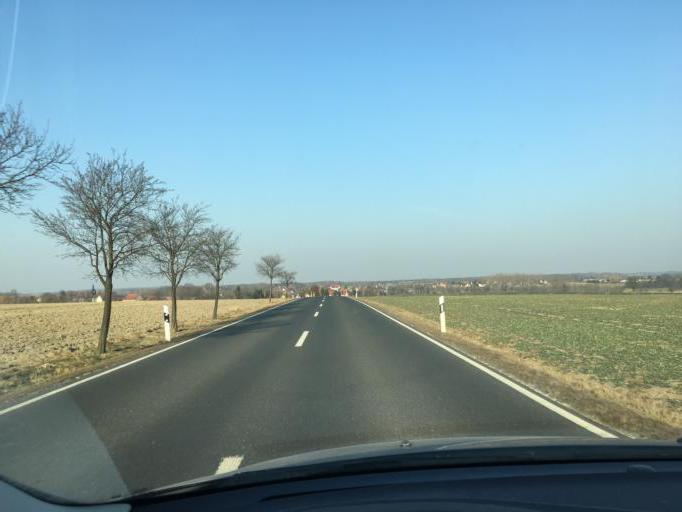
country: DE
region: Saxony
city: Kitzscher
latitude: 51.1157
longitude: 12.5851
